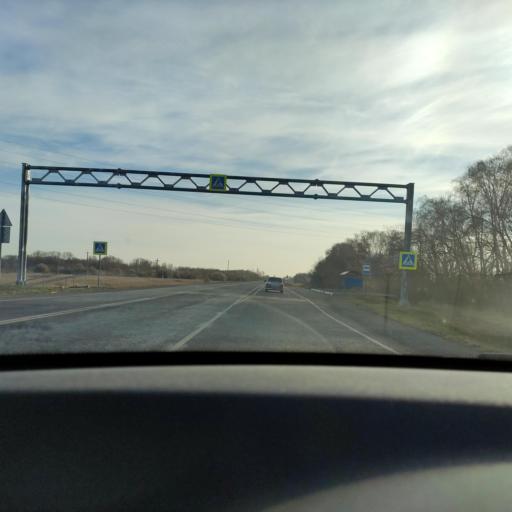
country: RU
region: Samara
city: Krasnoarmeyskoye
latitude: 52.7744
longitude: 50.0231
